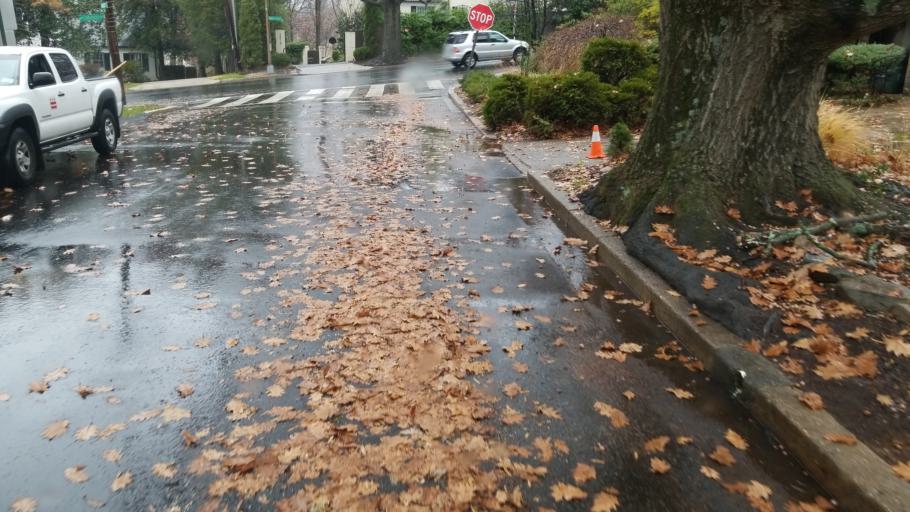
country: US
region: Maryland
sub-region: Montgomery County
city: Brookmont
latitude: 38.9321
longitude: -77.0963
